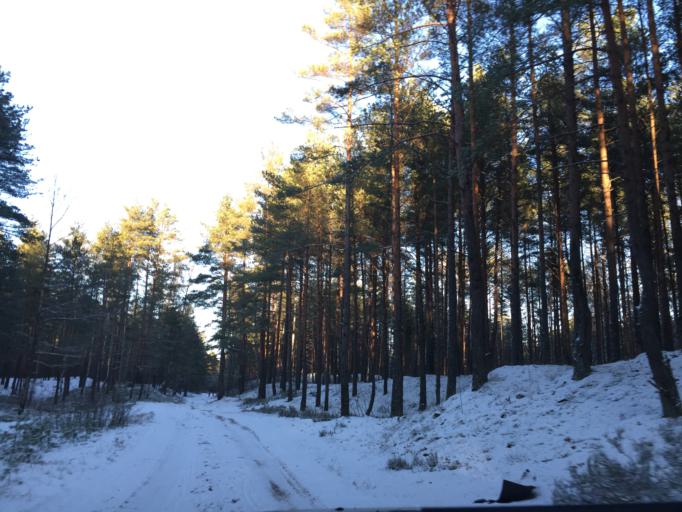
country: LV
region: Kekava
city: Balozi
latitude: 56.8809
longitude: 24.1222
